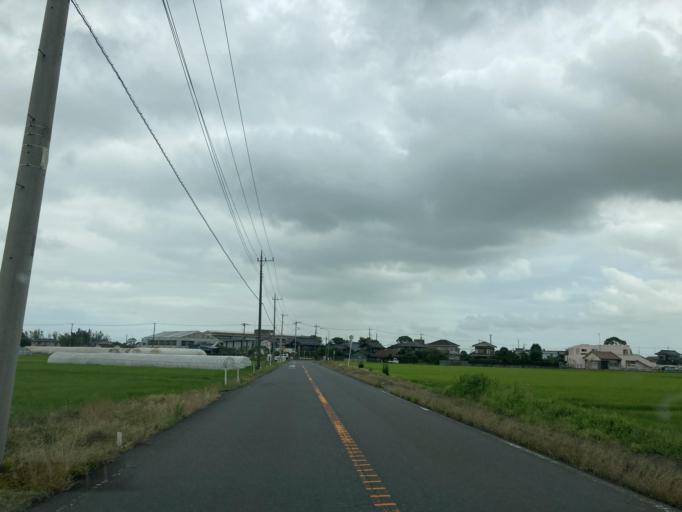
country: JP
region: Chiba
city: Omigawa
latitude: 35.8265
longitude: 140.5895
